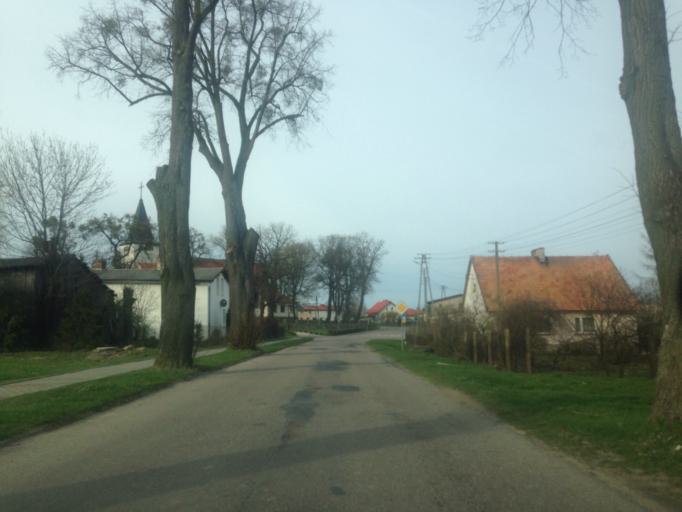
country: PL
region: Kujawsko-Pomorskie
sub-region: Powiat grudziadzki
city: Swiecie nad Osa
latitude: 53.4649
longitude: 19.1620
